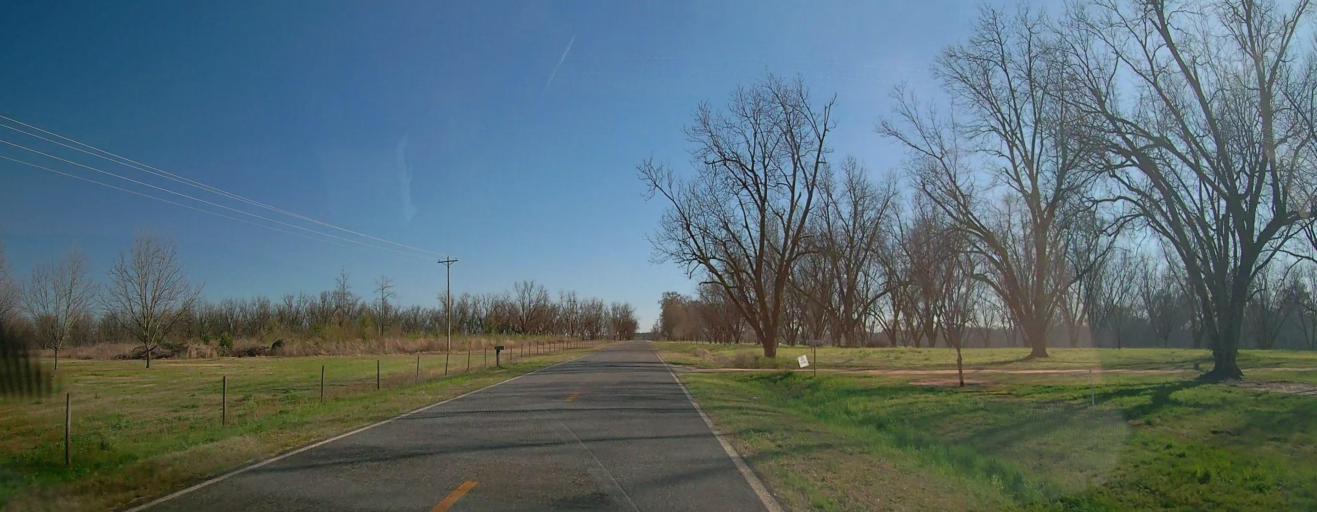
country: US
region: Georgia
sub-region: Peach County
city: Fort Valley
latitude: 32.6060
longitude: -83.8523
